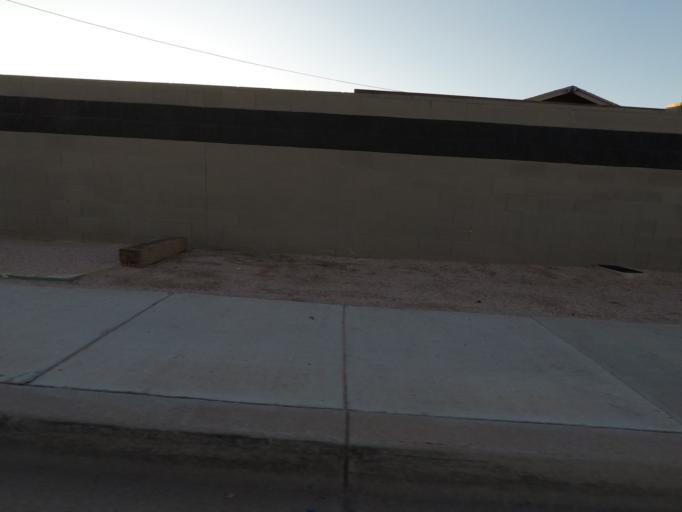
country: US
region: Arizona
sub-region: Maricopa County
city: Guadalupe
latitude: 33.3882
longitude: -111.9437
